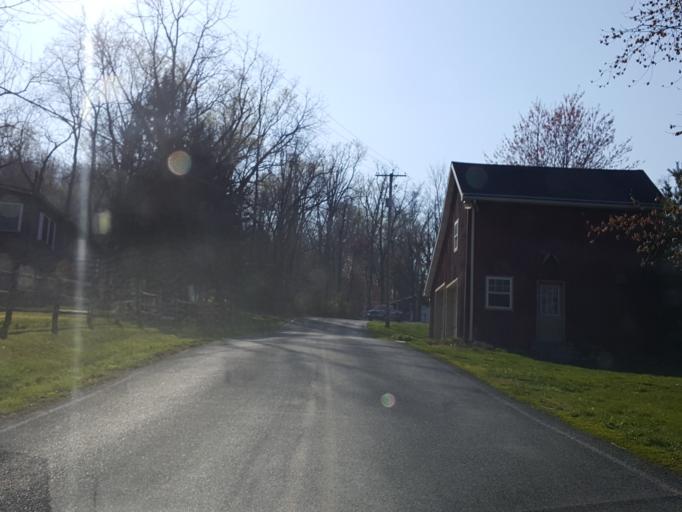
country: US
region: Pennsylvania
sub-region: Lebanon County
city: Annville
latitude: 40.2720
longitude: -76.5244
